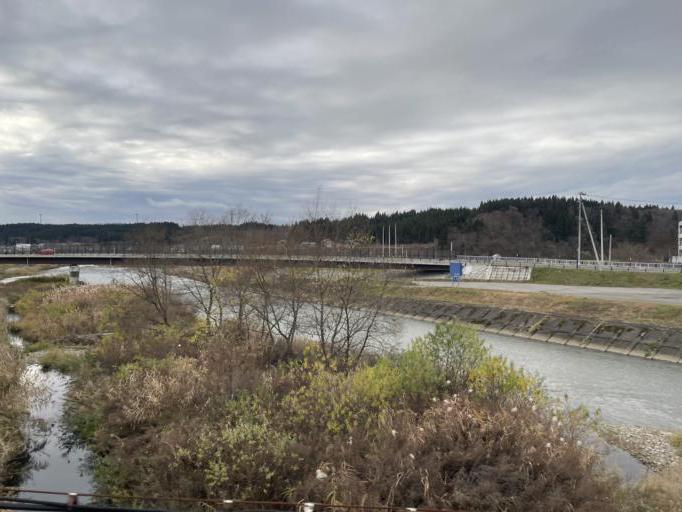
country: JP
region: Yamagata
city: Shinjo
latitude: 38.8624
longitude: 140.2578
